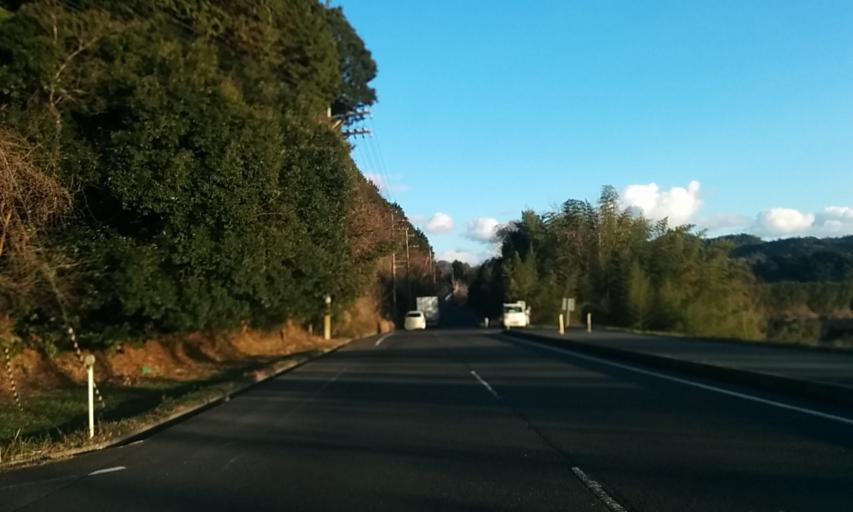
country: JP
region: Kyoto
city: Ayabe
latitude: 35.3103
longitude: 135.2631
